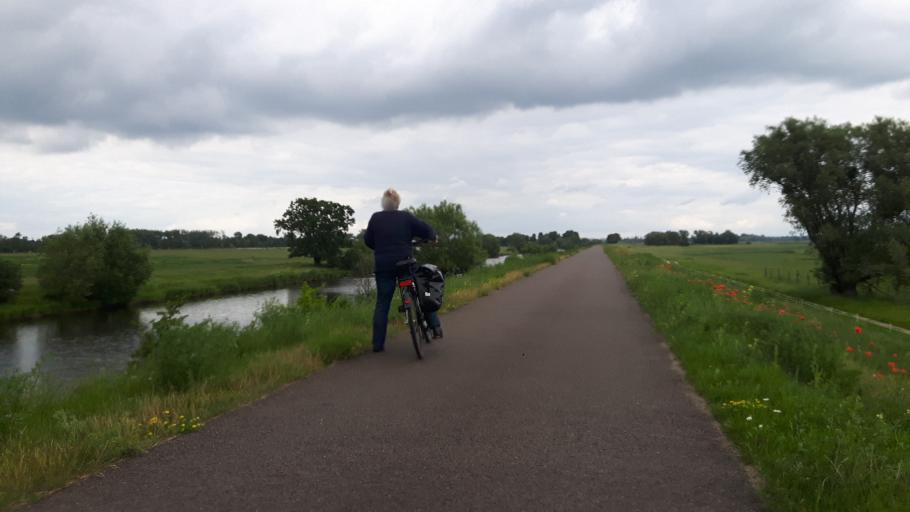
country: DE
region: Brandenburg
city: Meyenburg
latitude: 53.0280
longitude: 14.2496
